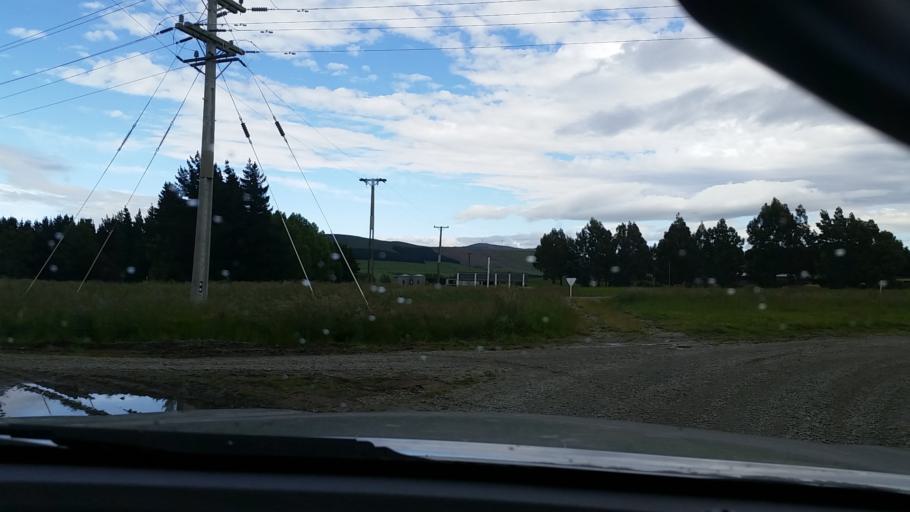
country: NZ
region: Southland
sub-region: Southland District
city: Winton
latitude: -45.7651
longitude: 168.4112
